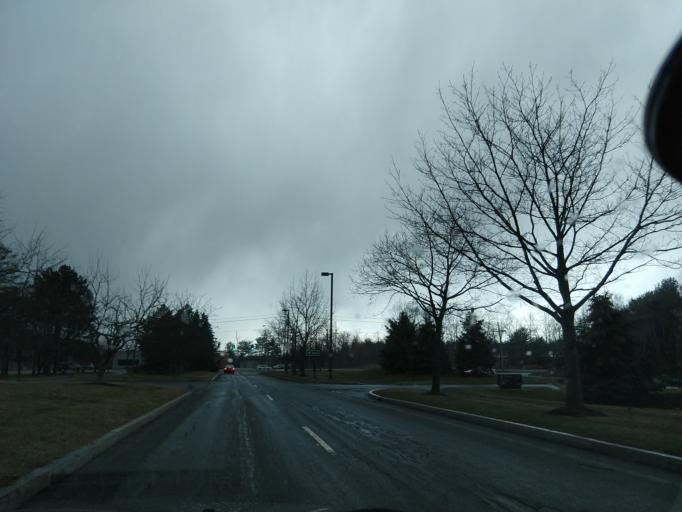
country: US
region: New York
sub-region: Tompkins County
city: Lansing
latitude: 42.4874
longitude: -76.4660
